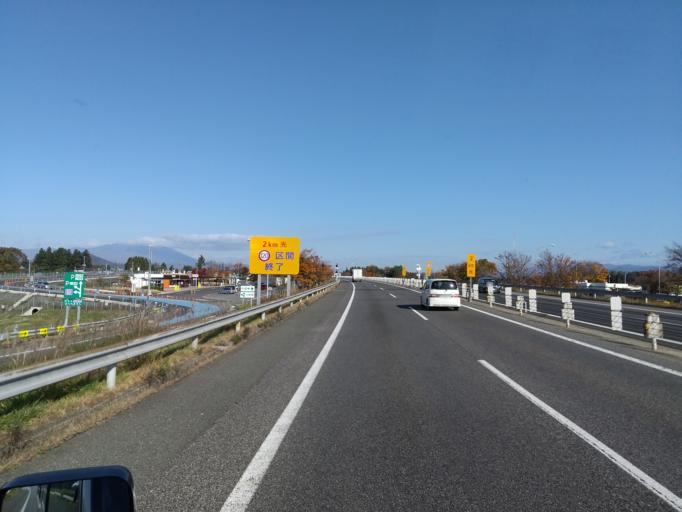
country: JP
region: Iwate
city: Morioka-shi
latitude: 39.6170
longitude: 141.1298
